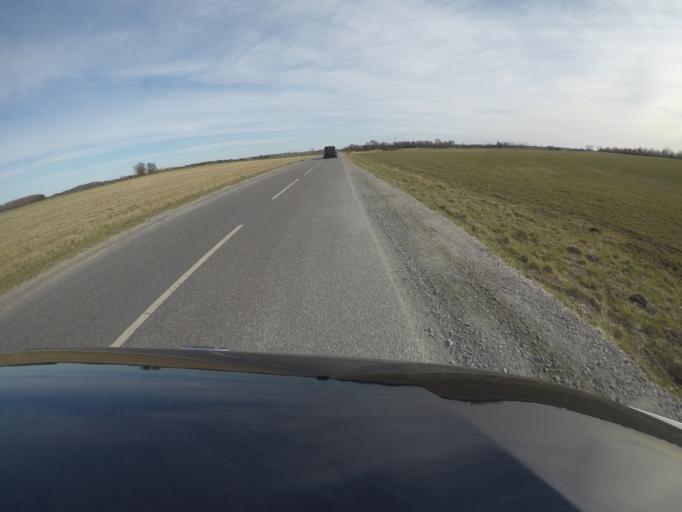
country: DK
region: Capital Region
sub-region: Halsnaes Kommune
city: Liseleje
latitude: 55.9823
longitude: 11.9499
